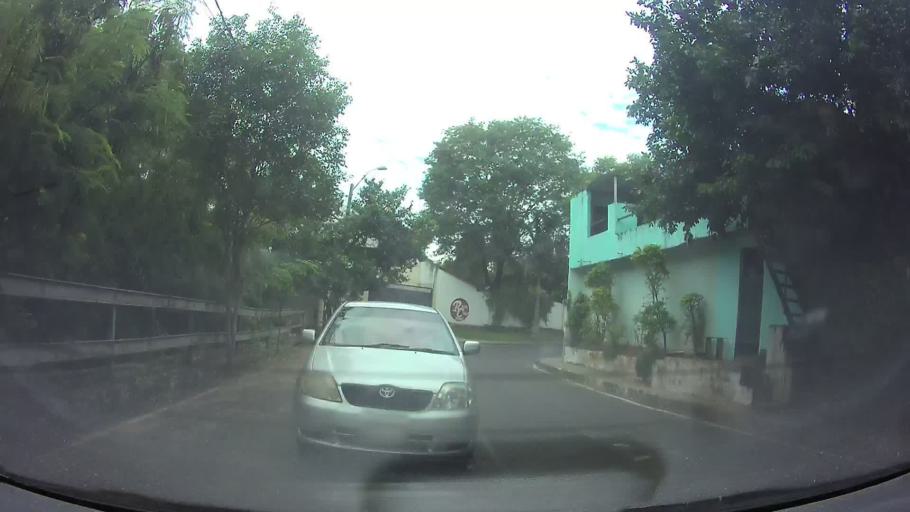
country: PY
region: Asuncion
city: Asuncion
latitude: -25.3026
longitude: -57.5959
